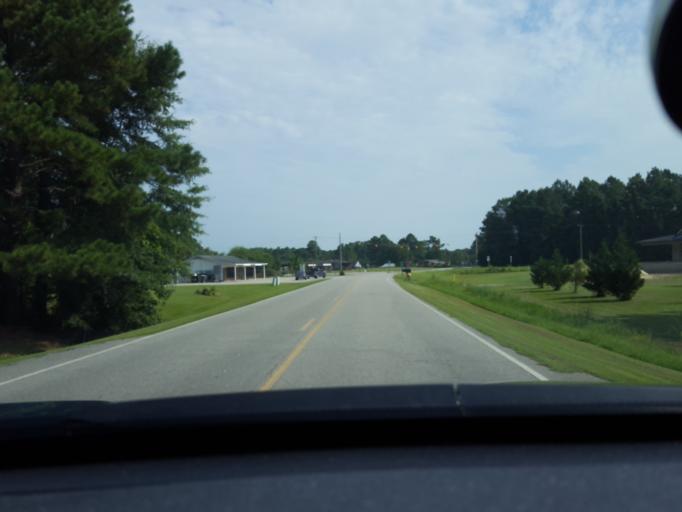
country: US
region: North Carolina
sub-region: Washington County
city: Plymouth
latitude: 35.8905
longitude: -76.7039
